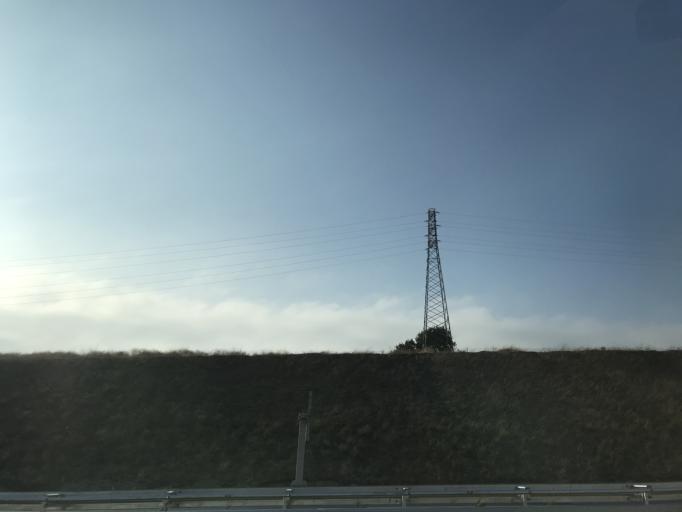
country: TR
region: Balikesir
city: Gobel
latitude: 39.9751
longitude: 28.1681
